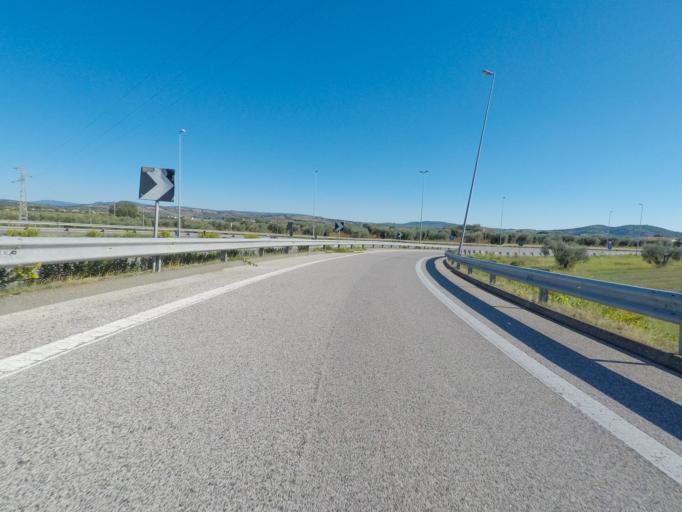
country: IT
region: Tuscany
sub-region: Provincia di Grosseto
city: Grosseto
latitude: 42.7720
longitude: 11.1456
